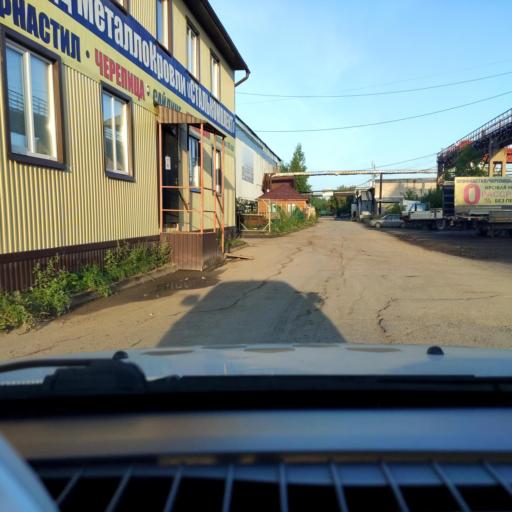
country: RU
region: Perm
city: Froly
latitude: 57.9545
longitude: 56.2558
